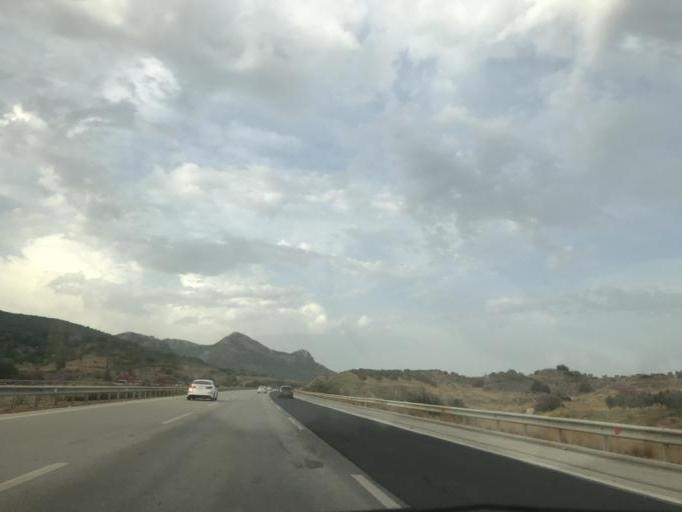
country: TR
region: Adana
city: Ceyhan
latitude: 37.0102
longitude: 35.9613
